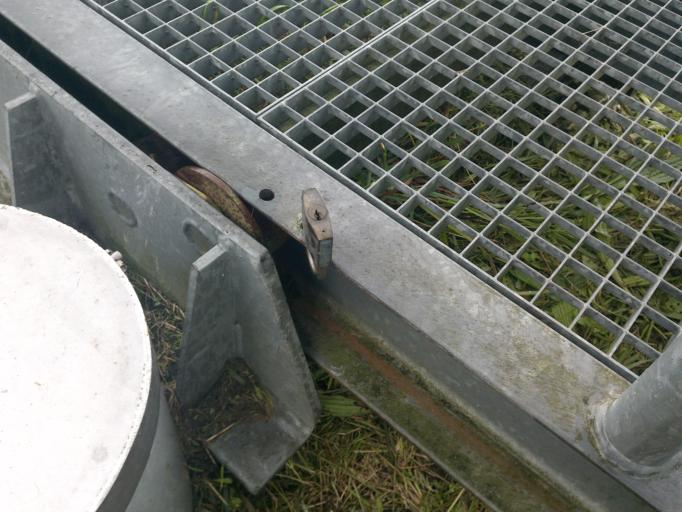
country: NL
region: Friesland
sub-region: Gemeente Boarnsterhim
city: Aldeboarn
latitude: 53.0844
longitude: 5.8790
